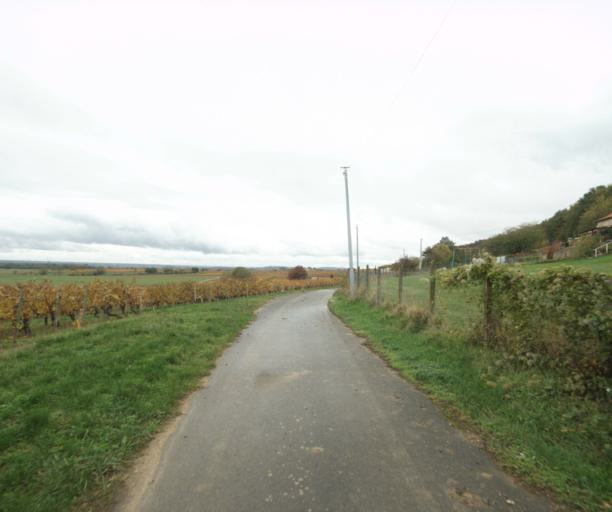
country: FR
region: Bourgogne
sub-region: Departement de Saone-et-Loire
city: Saint-Martin-Belle-Roche
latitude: 46.4686
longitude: 4.8475
